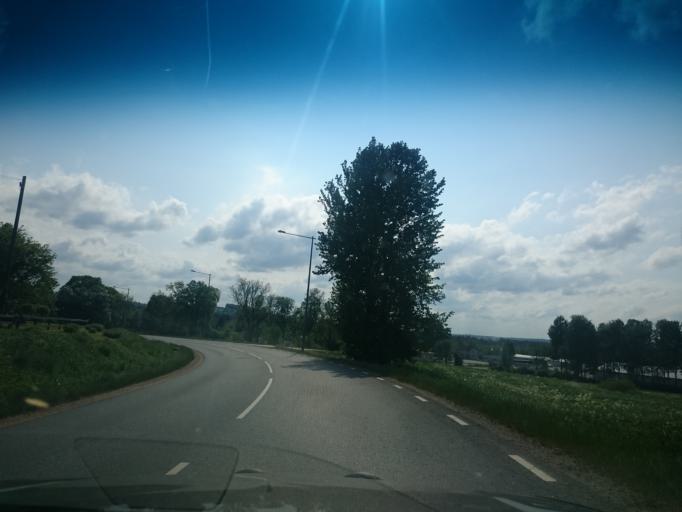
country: SE
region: Joenkoeping
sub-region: Vetlanda Kommun
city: Landsbro
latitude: 57.3856
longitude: 14.9612
